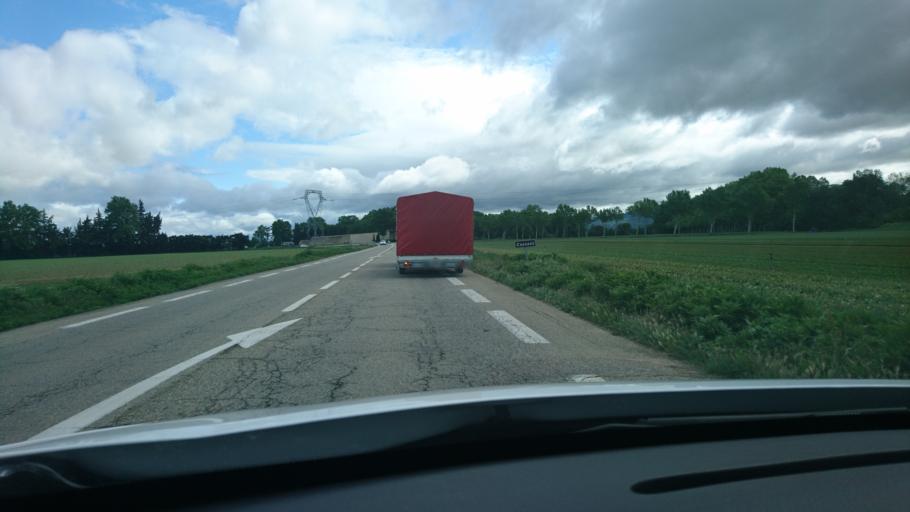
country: FR
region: Provence-Alpes-Cote d'Azur
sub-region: Departement du Vaucluse
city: Jonquieres
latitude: 44.1233
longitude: 4.9313
